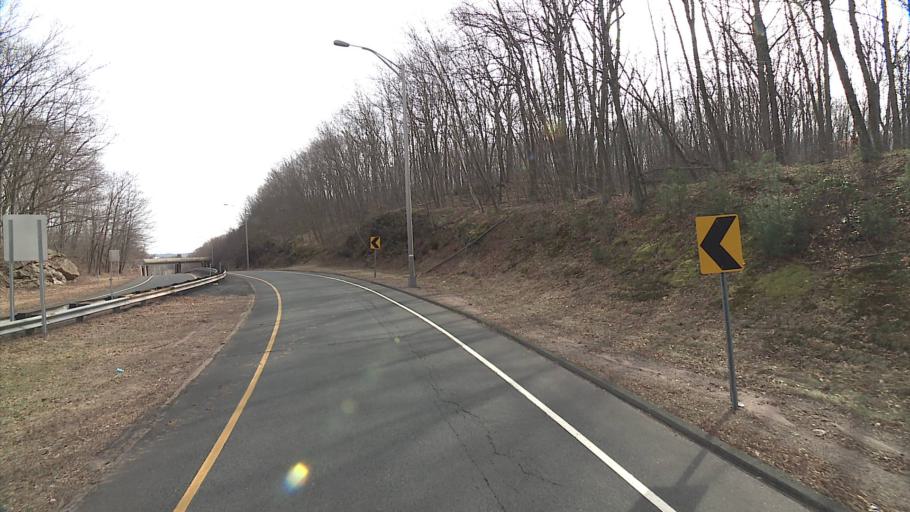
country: US
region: Connecticut
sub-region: Middlesex County
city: Higganum
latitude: 41.5125
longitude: -72.6005
